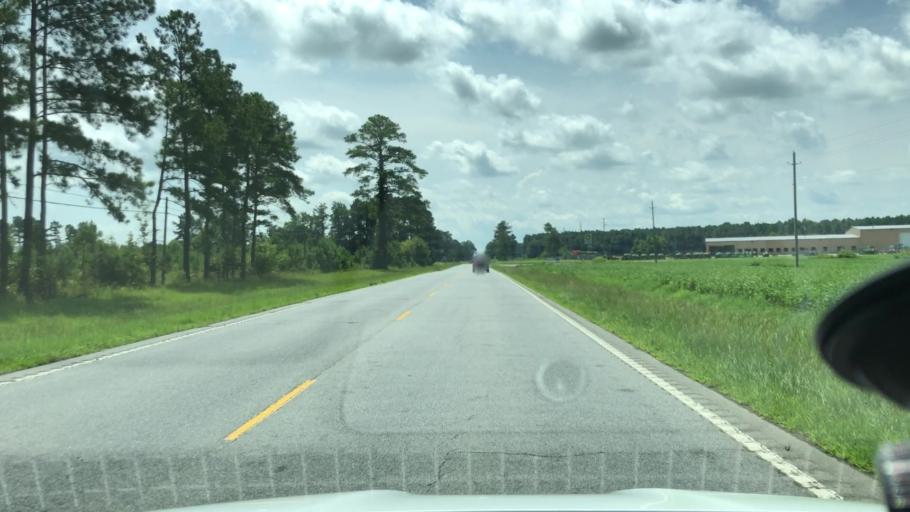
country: US
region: North Carolina
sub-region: Beaufort County
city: Washington
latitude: 35.6535
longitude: -77.0712
